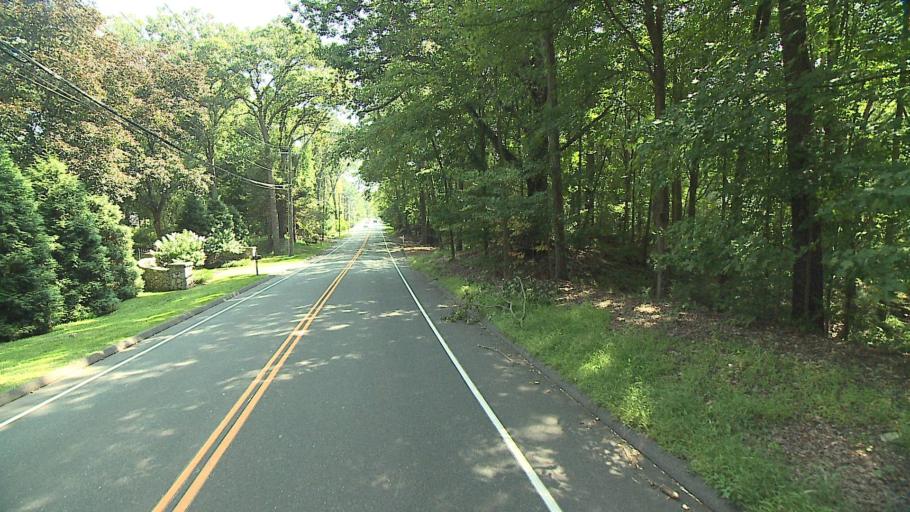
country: US
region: Connecticut
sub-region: Fairfield County
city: Westport
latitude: 41.1778
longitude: -73.3636
